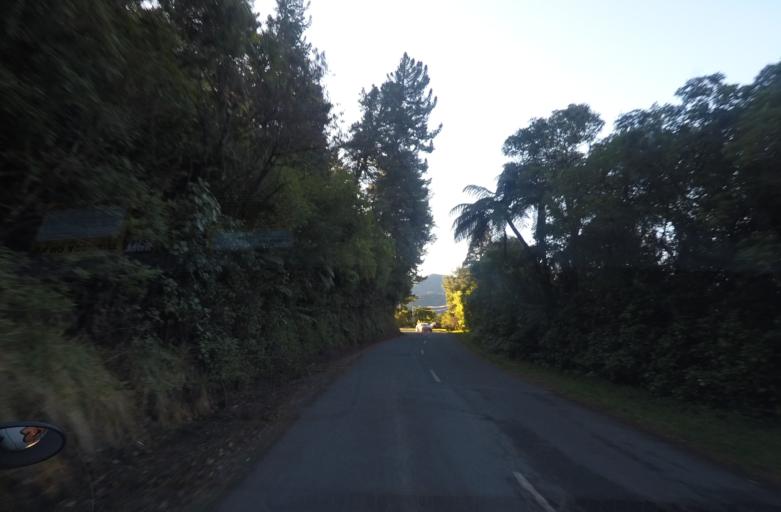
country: NZ
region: Marlborough
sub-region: Marlborough District
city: Picton
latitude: -41.2699
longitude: 173.9479
